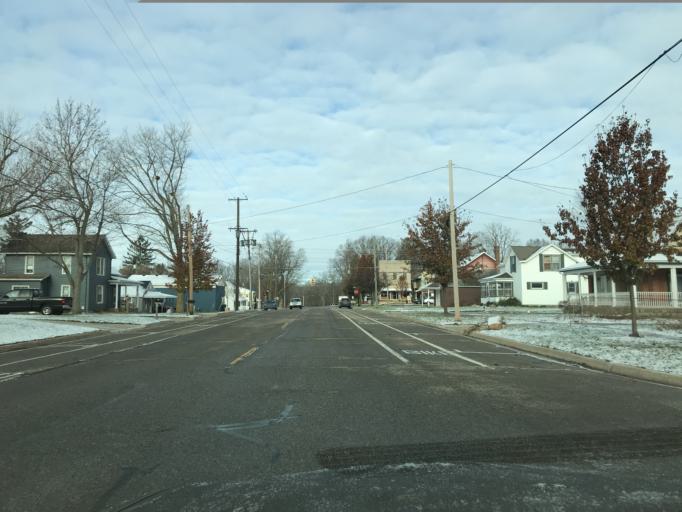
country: US
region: Michigan
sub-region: Eaton County
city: Dimondale
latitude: 42.6449
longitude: -84.6478
